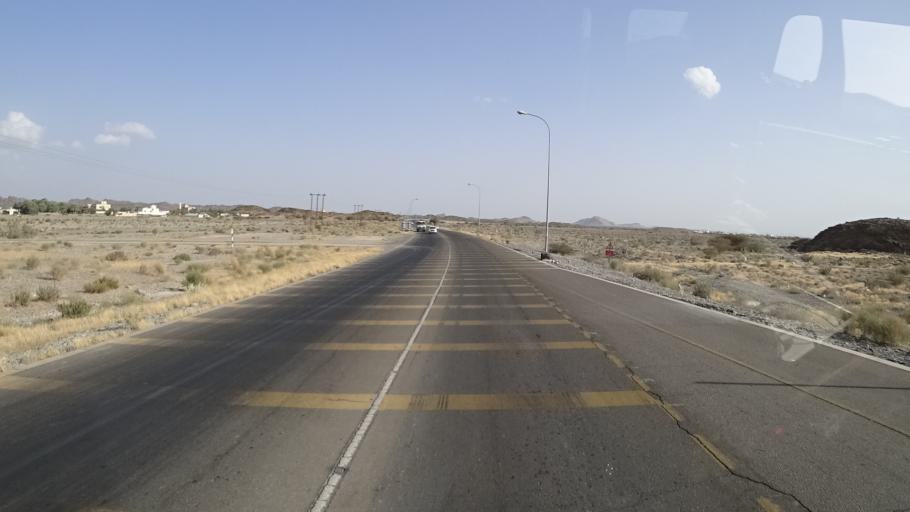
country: OM
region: Muhafazat ad Dakhiliyah
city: Izki
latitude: 22.8797
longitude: 57.7548
